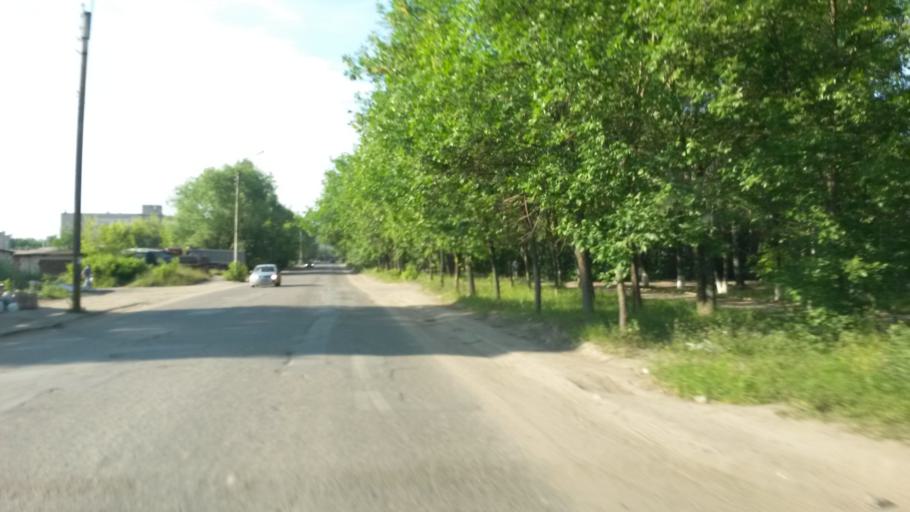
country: RU
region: Ivanovo
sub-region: Gorod Ivanovo
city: Ivanovo
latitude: 56.9595
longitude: 40.9851
